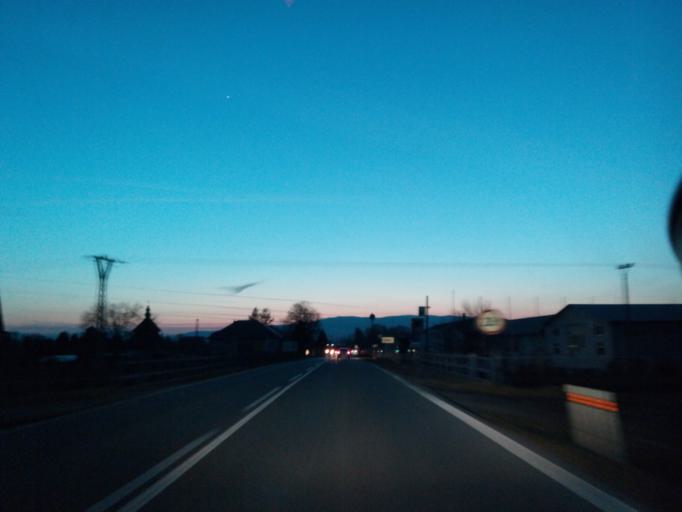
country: SK
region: Kosicky
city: Secovce
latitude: 48.6990
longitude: 21.7128
